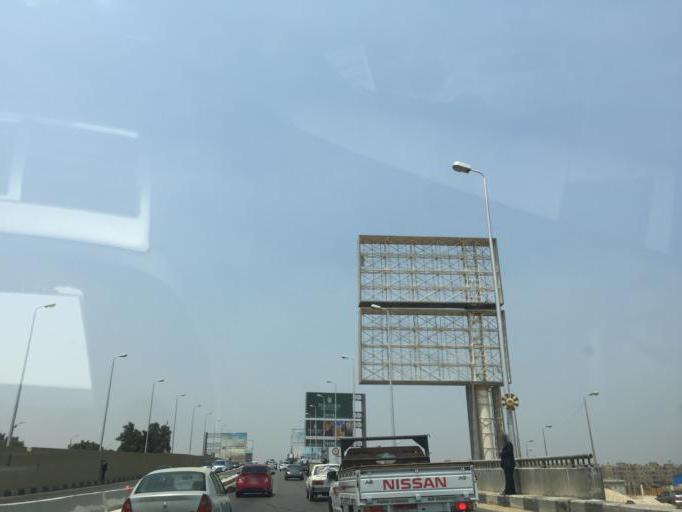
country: EG
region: Muhafazat al Qalyubiyah
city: Al Khankah
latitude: 30.0800
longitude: 31.3837
